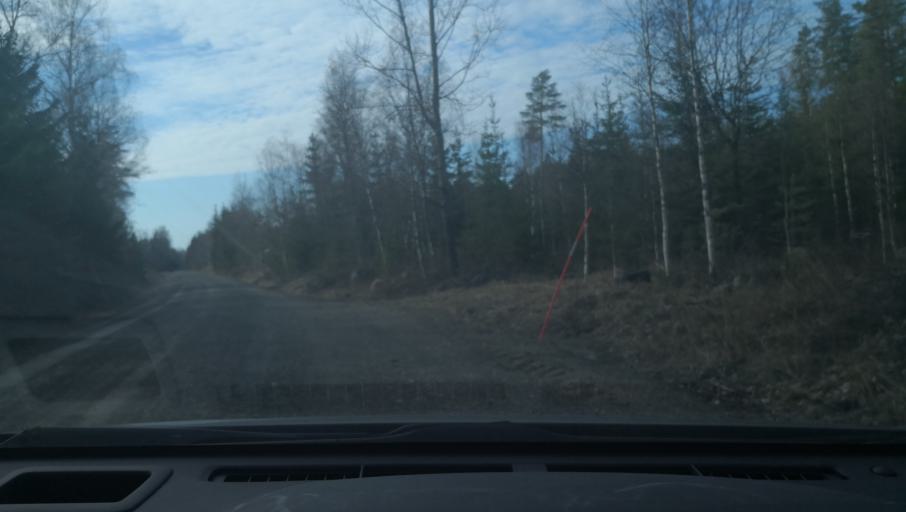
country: SE
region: Uppsala
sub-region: Heby Kommun
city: Heby
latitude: 59.8551
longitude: 16.8657
